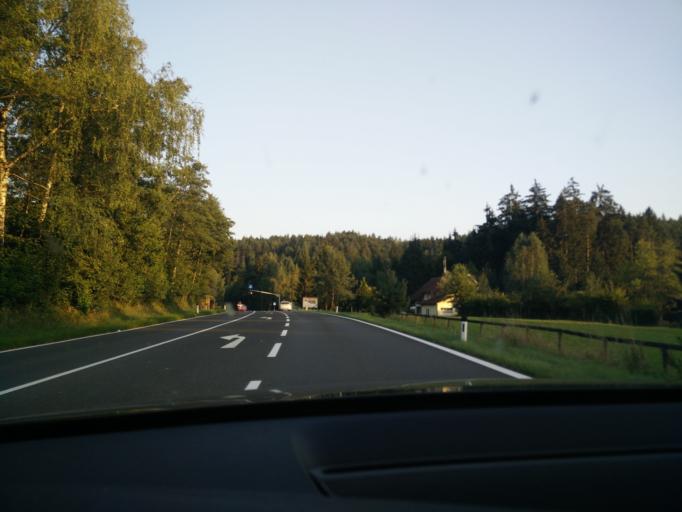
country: AT
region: Carinthia
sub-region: Politischer Bezirk Villach Land
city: Finkenstein am Faaker See
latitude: 46.5915
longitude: 13.8924
